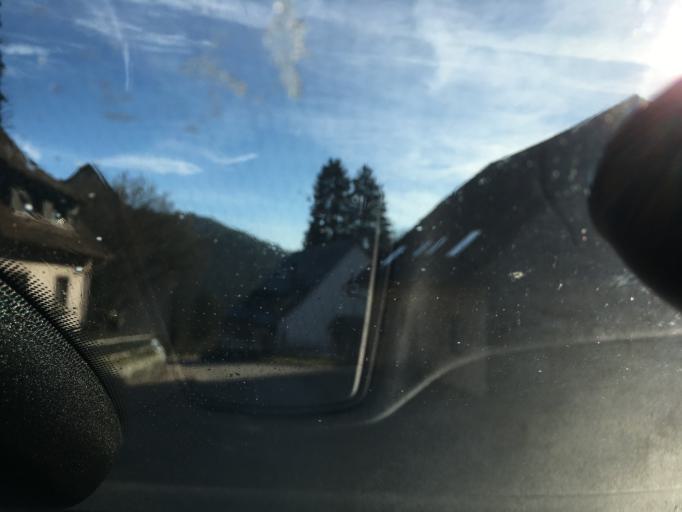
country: DE
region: Baden-Wuerttemberg
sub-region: Freiburg Region
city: Gorwihl
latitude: 47.6256
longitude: 8.0851
